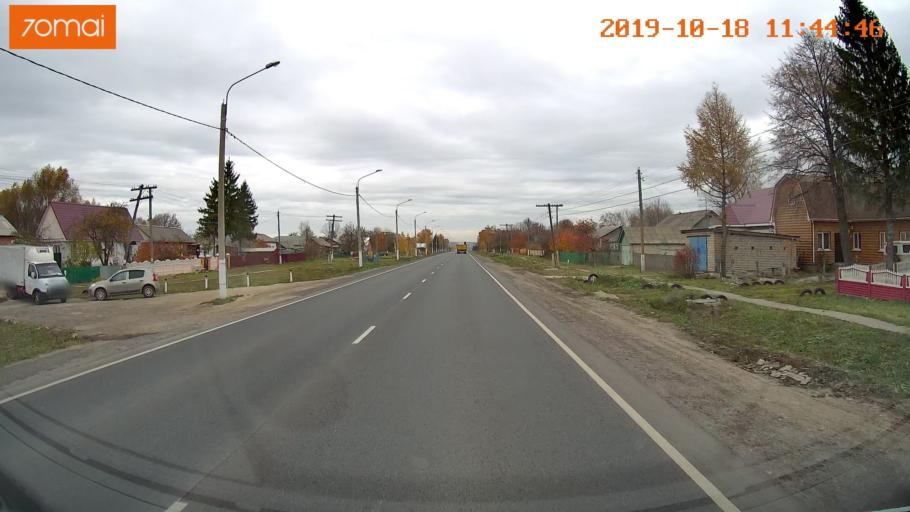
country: RU
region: Rjazan
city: Mikhaylov
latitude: 54.2049
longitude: 38.9619
